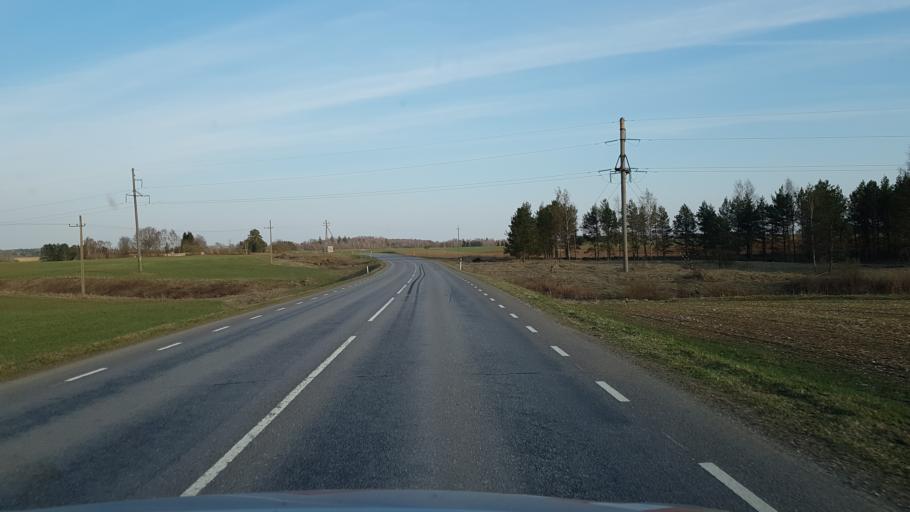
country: EE
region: Laeaene-Virumaa
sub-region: Vinni vald
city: Vinni
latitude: 59.3184
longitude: 26.4387
